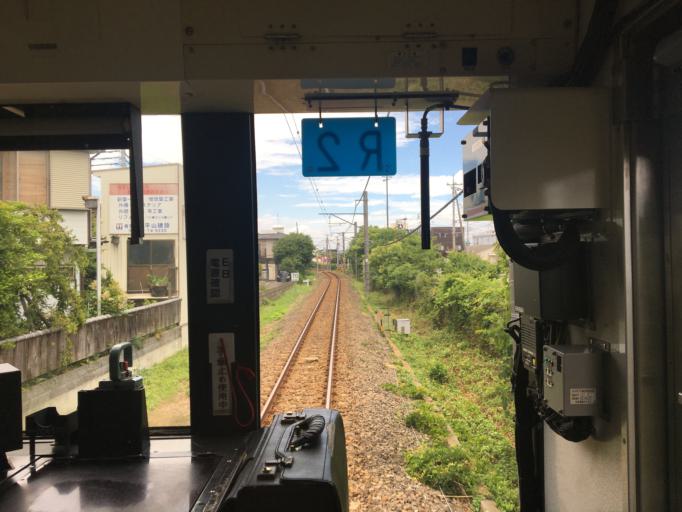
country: JP
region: Kanagawa
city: Atsugi
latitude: 35.4005
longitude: 139.3807
